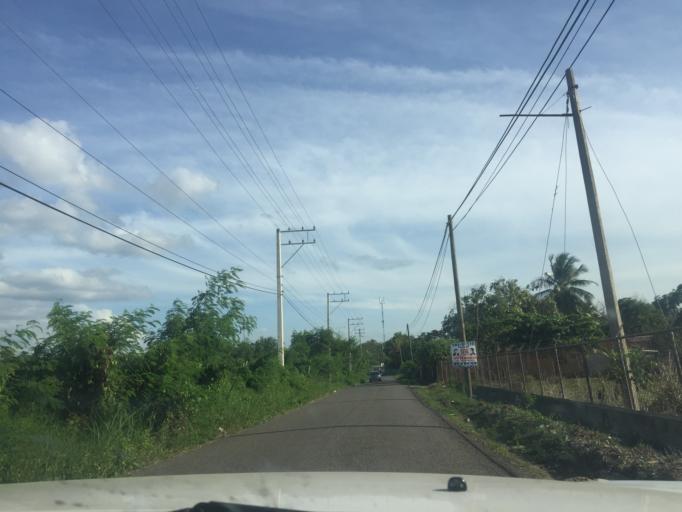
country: DO
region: Santiago
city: Tamboril
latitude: 19.4830
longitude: -70.6374
